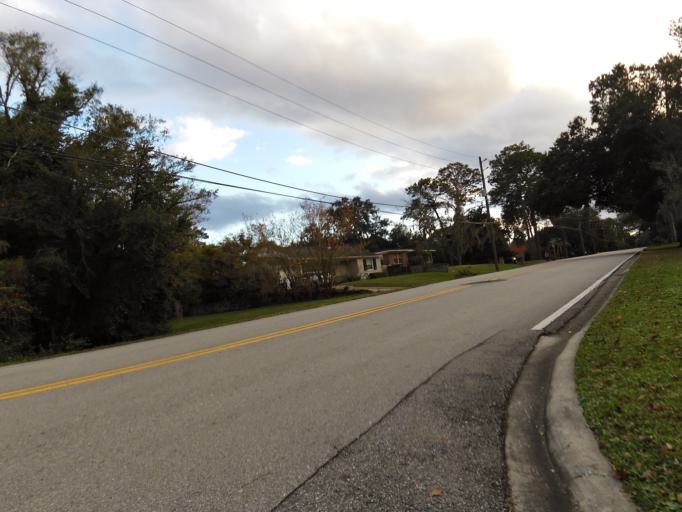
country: US
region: Florida
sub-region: Duval County
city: Jacksonville
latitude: 30.2839
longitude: -81.6566
